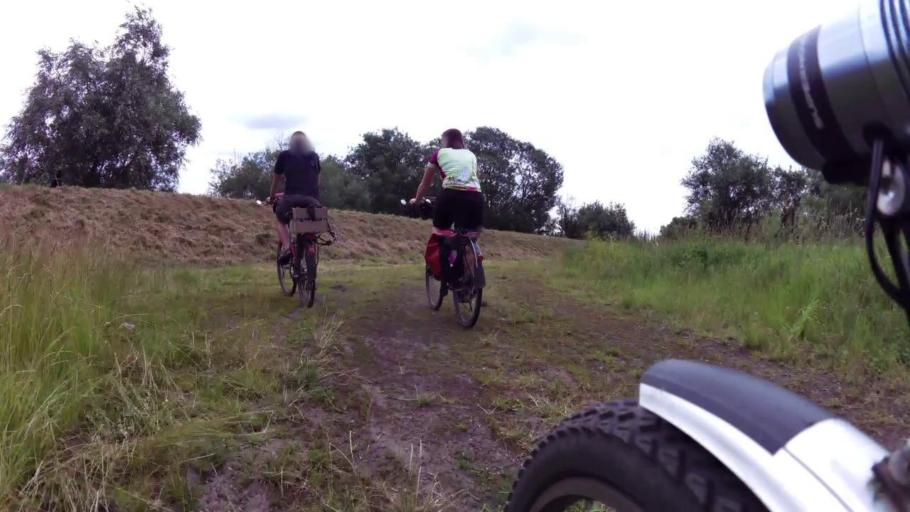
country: PL
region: West Pomeranian Voivodeship
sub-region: Powiat policki
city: Police
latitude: 53.6062
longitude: 14.5712
